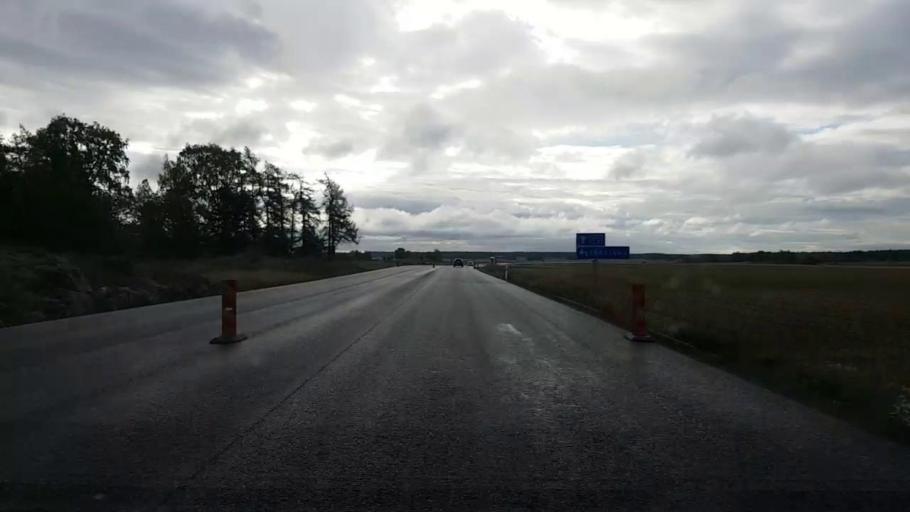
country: SE
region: Uppsala
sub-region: Enkopings Kommun
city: Irsta
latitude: 59.7551
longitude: 16.9356
